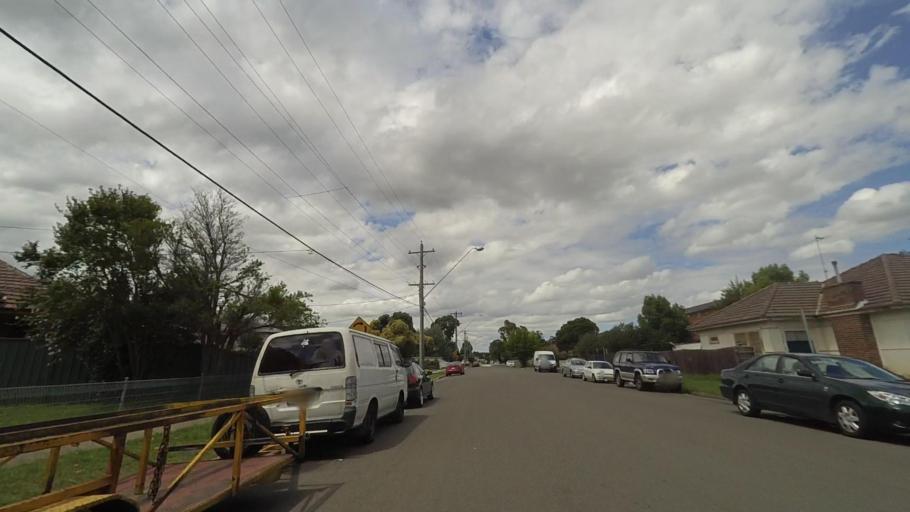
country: AU
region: New South Wales
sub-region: Fairfield
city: Fairfield Heights
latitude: -33.8664
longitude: 150.9525
